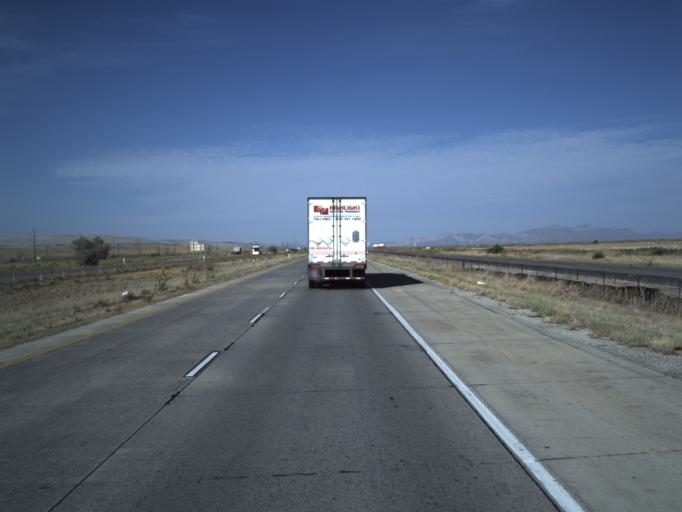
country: US
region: Utah
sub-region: Salt Lake County
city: Magna
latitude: 40.7711
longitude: -112.0769
